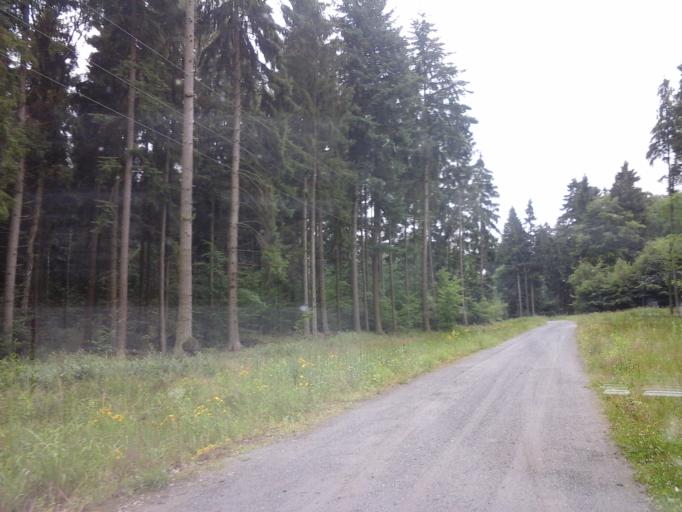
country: PL
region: West Pomeranian Voivodeship
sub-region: Powiat choszczenski
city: Krzecin
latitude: 53.0100
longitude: 15.4783
